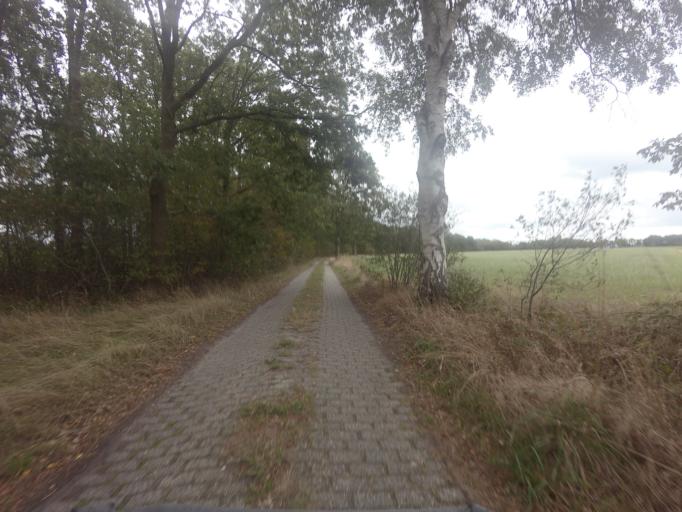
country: NL
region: Friesland
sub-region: Gemeente Weststellingwerf
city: Noordwolde
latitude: 52.9329
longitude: 6.1744
